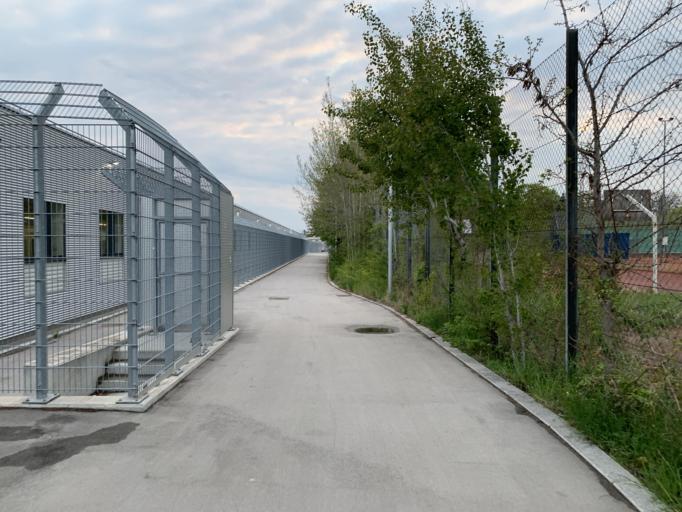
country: AT
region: Lower Austria
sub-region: Politischer Bezirk Wien-Umgebung
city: Leopoldsdorf
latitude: 48.1439
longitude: 16.3943
